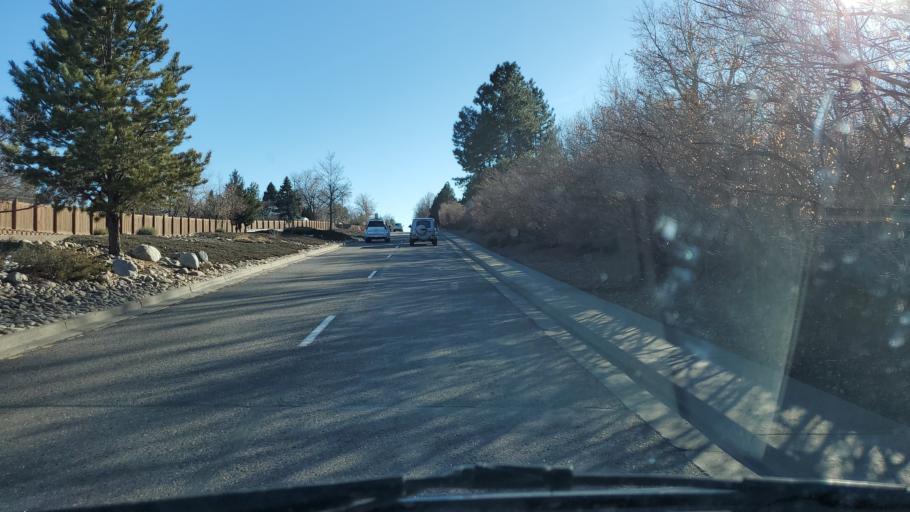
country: US
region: Colorado
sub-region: Arapahoe County
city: Castlewood
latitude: 39.5898
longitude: -104.9043
